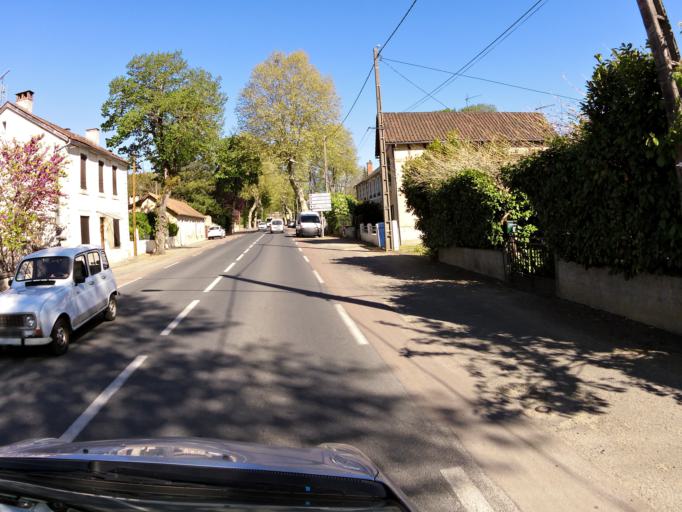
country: FR
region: Aquitaine
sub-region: Departement de la Dordogne
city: Montignac
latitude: 45.0647
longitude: 1.1711
